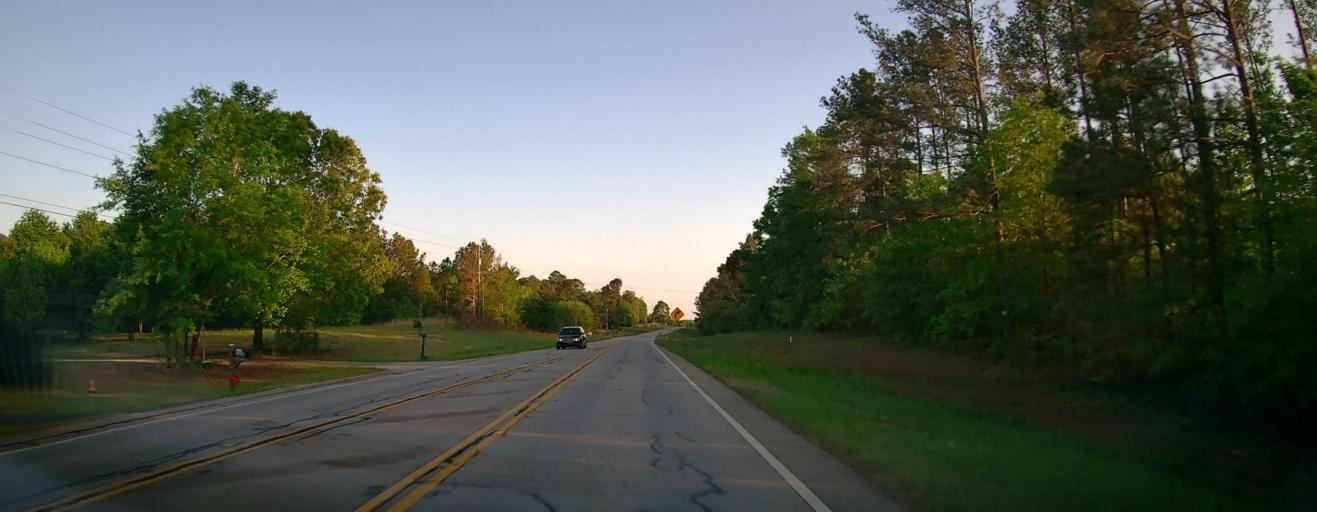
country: US
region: Georgia
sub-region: Newton County
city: Oakwood
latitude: 33.5141
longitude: -83.9482
